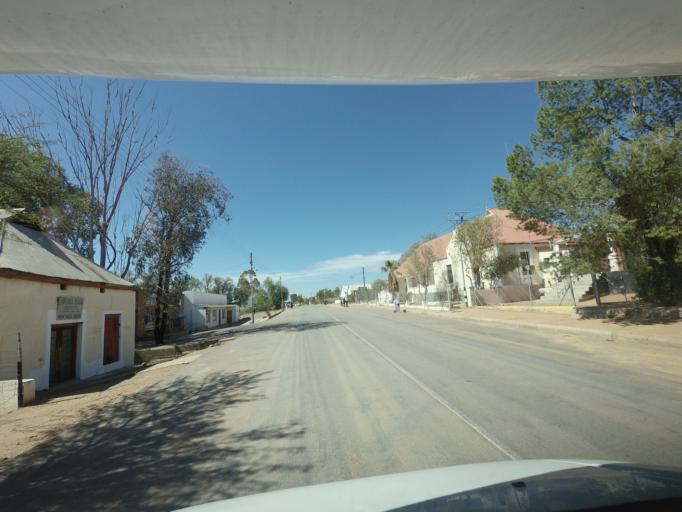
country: ZA
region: Northern Cape
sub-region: Namakwa District Municipality
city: Garies
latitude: -30.5594
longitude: 17.9902
